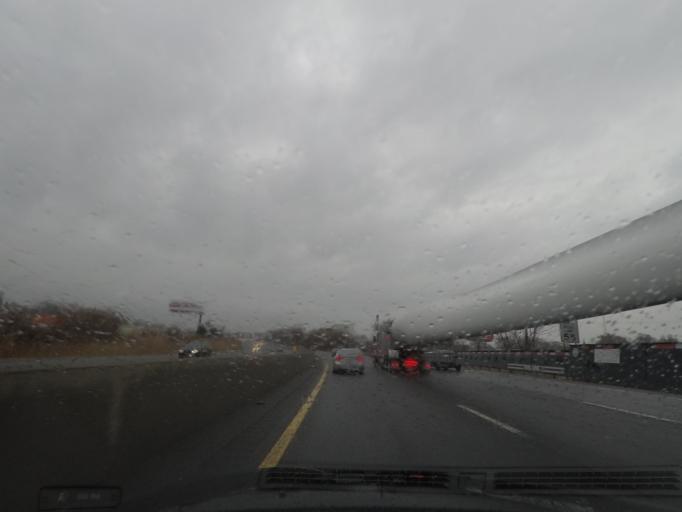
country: US
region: New York
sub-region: Albany County
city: West Albany
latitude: 42.6860
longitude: -73.7916
